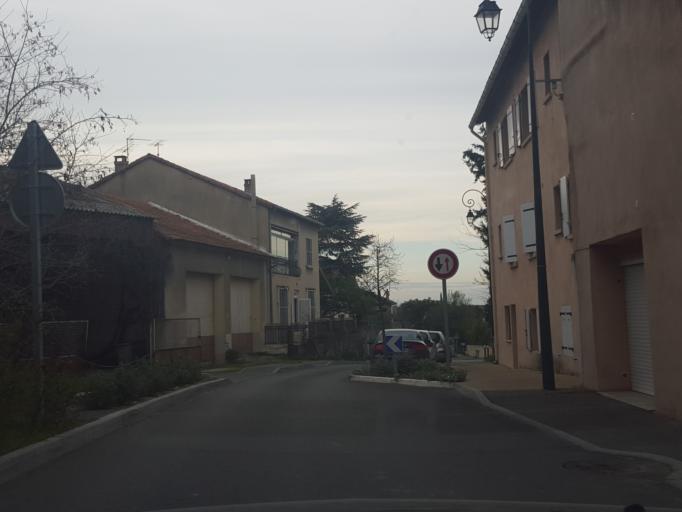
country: FR
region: Provence-Alpes-Cote d'Azur
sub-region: Departement du Vaucluse
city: Chateauneuf-de-Gadagne
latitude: 43.9297
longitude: 4.9461
